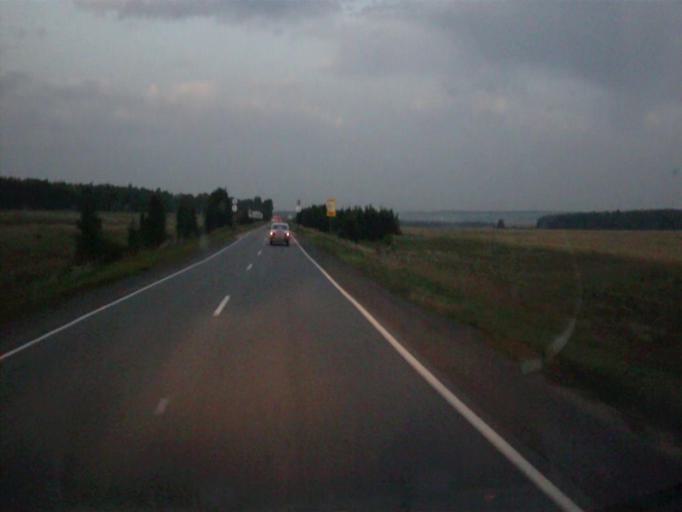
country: RU
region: Chelyabinsk
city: Argayash
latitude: 55.2089
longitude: 60.8371
